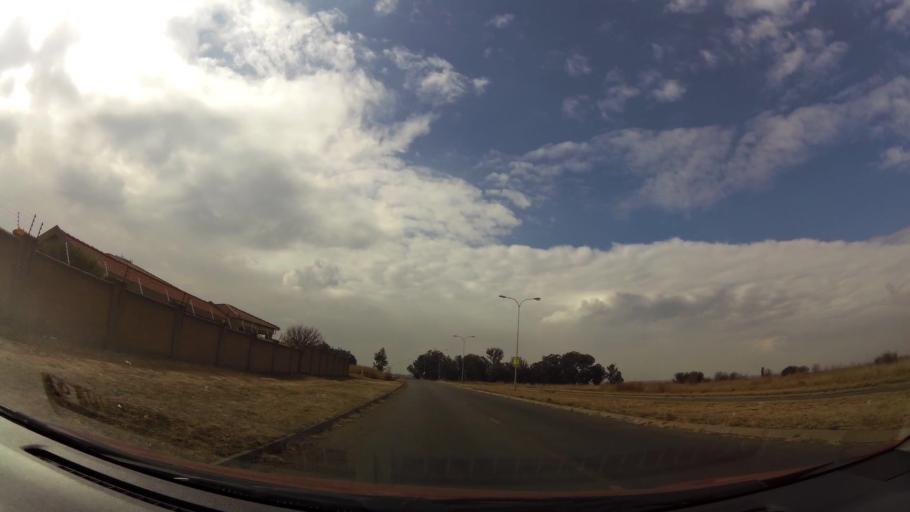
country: ZA
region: Gauteng
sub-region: Sedibeng District Municipality
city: Vanderbijlpark
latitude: -26.7285
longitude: 27.8706
